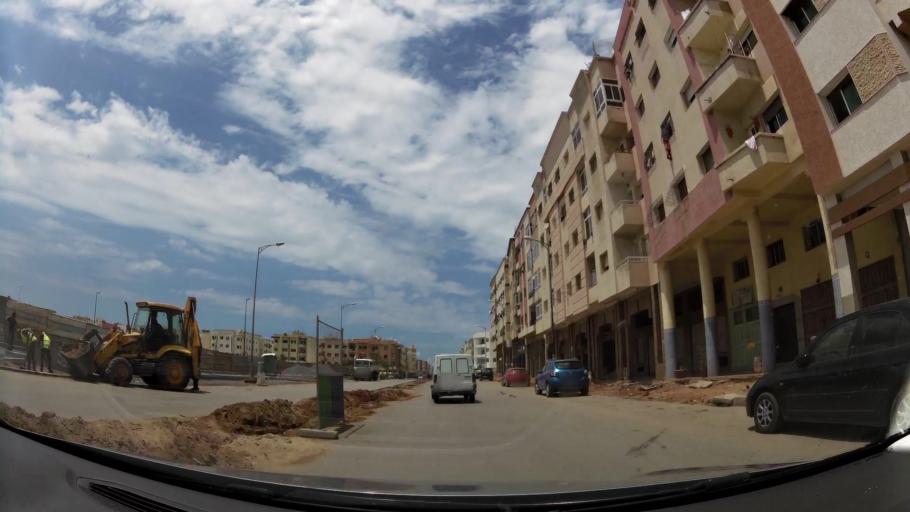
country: MA
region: Rabat-Sale-Zemmour-Zaer
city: Sale
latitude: 34.0609
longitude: -6.8039
